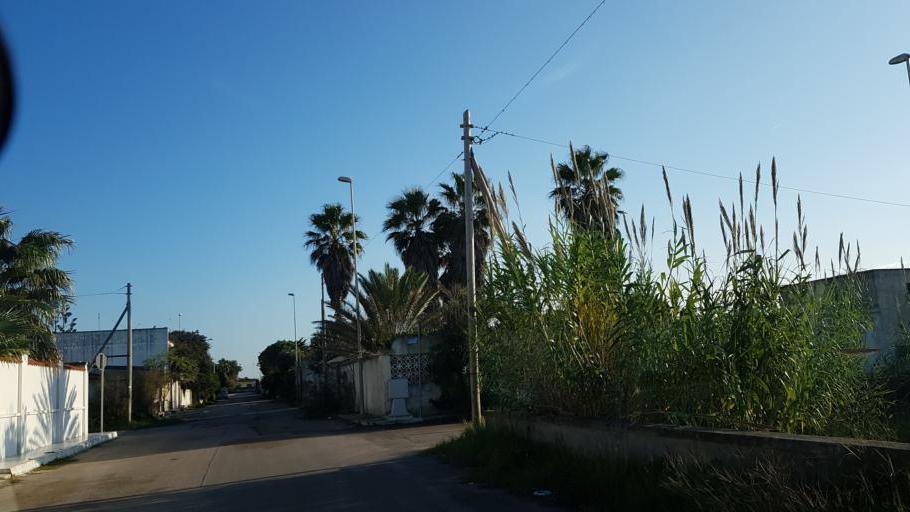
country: IT
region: Apulia
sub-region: Provincia di Brindisi
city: Torchiarolo
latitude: 40.5138
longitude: 18.0976
